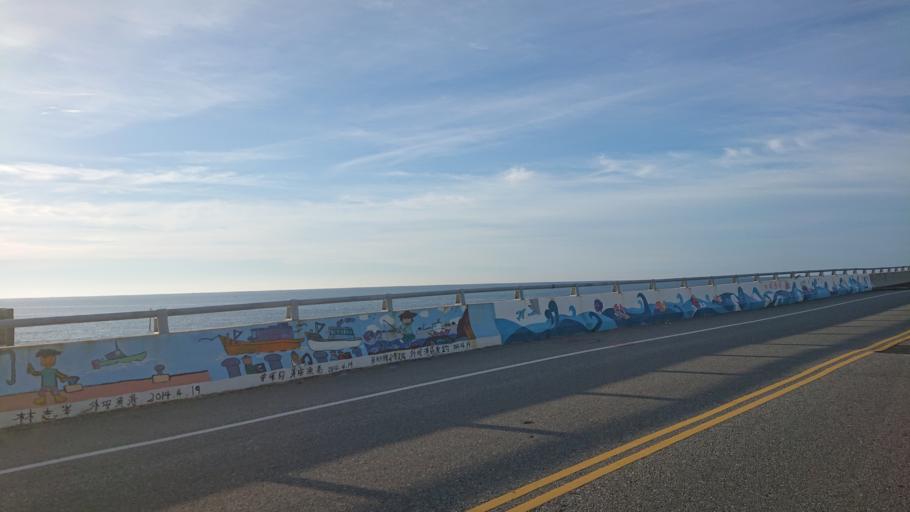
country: TW
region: Taiwan
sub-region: Penghu
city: Ma-kung
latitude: 23.6415
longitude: 119.5412
